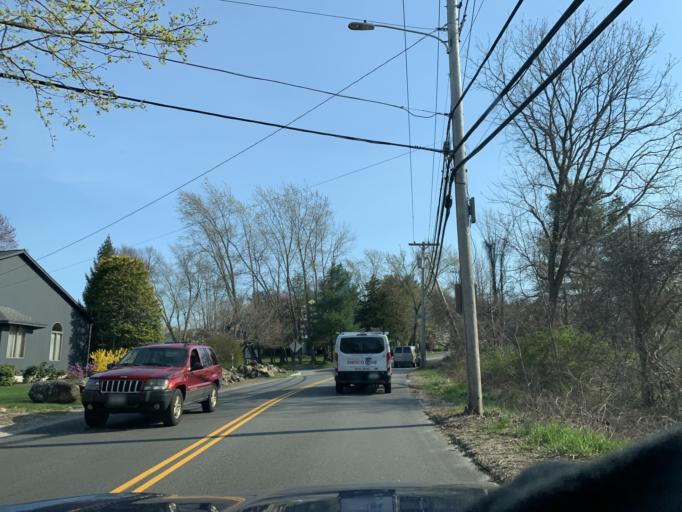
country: US
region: Rhode Island
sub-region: Kent County
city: West Warwick
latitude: 41.7548
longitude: -71.4980
